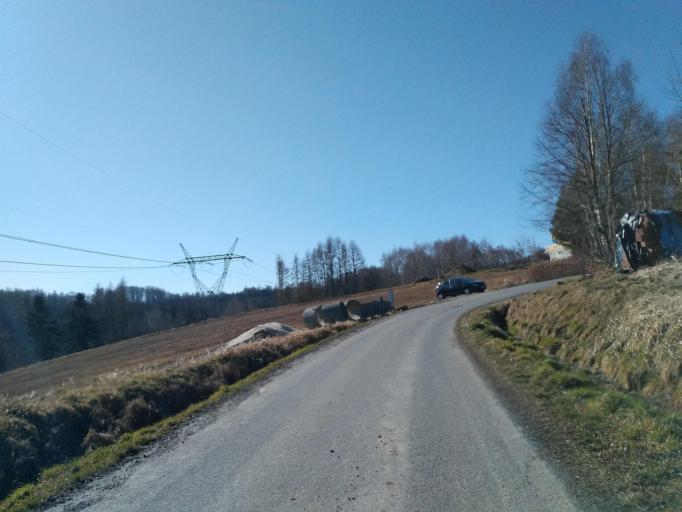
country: PL
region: Subcarpathian Voivodeship
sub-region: Powiat strzyzowski
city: Babica
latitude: 49.9521
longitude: 21.8890
